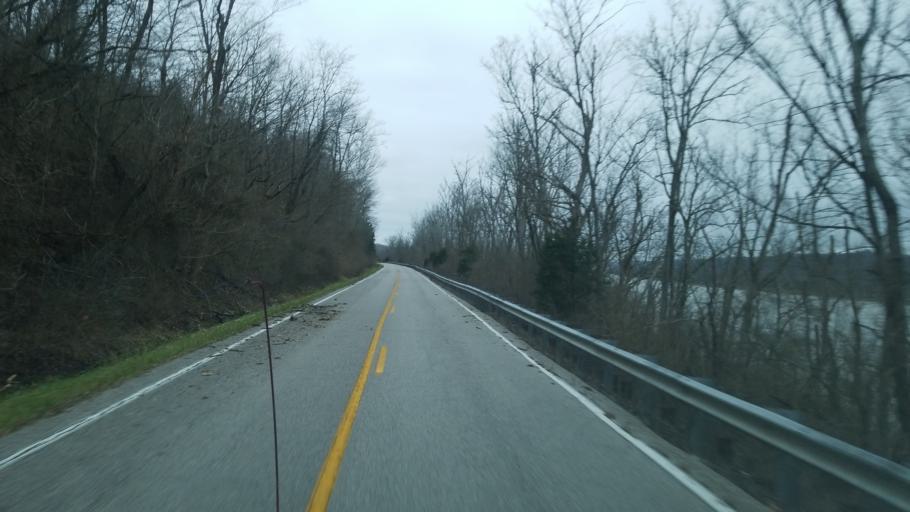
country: US
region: Kentucky
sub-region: Bracken County
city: Augusta
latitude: 38.7662
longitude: -84.0540
